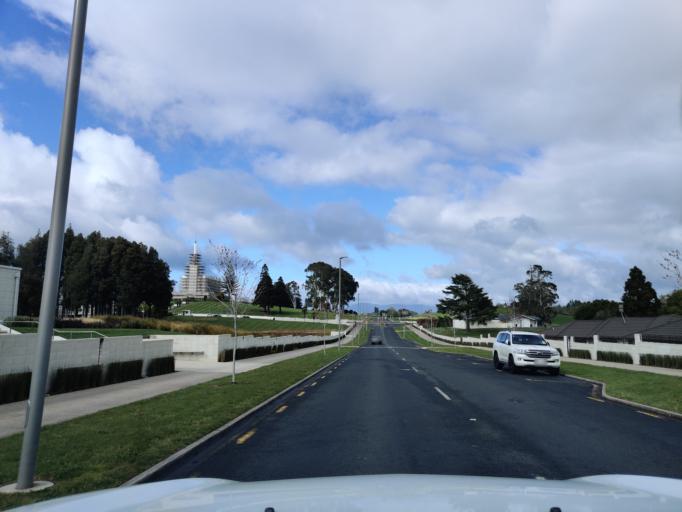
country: NZ
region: Waikato
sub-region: Hamilton City
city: Hamilton
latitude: -37.8230
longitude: 175.2255
